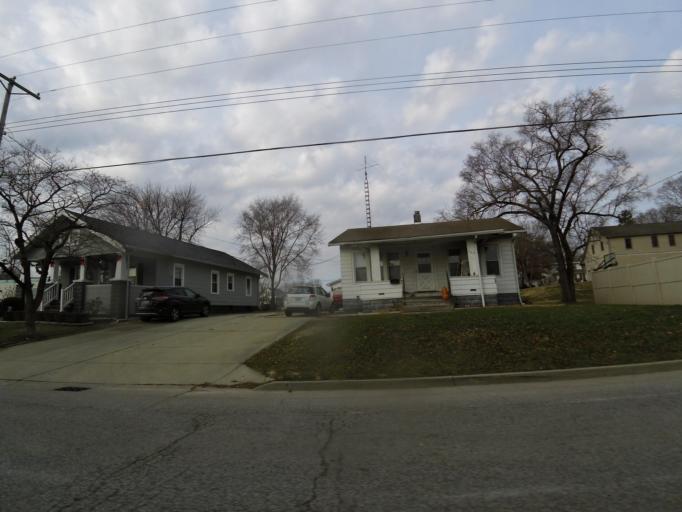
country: US
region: Illinois
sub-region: Christian County
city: Pana
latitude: 39.3806
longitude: -89.0816
